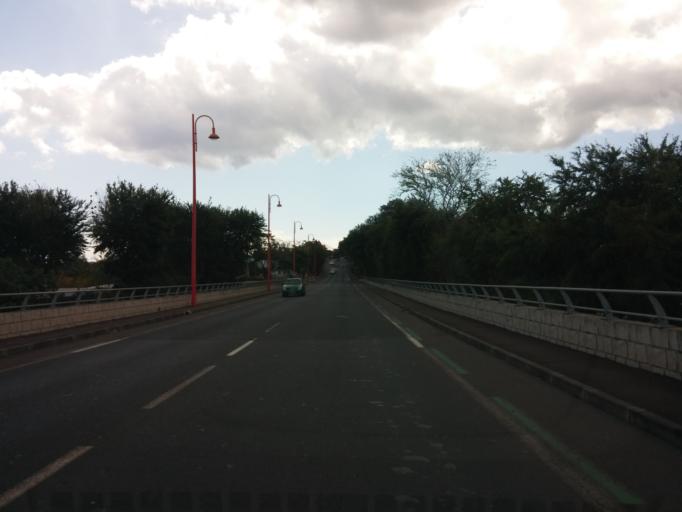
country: RE
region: Reunion
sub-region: Reunion
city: La Possession
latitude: -20.9396
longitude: 55.3312
